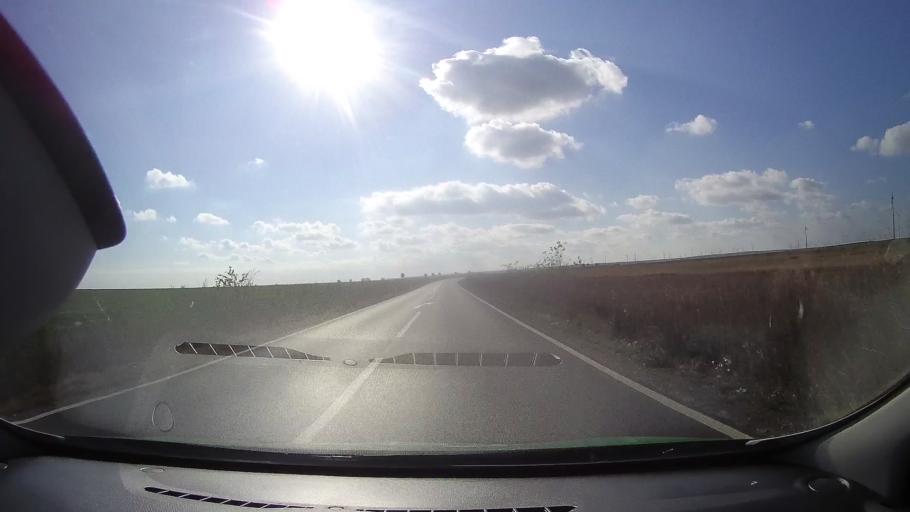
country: RO
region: Constanta
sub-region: Comuna Mihai Viteazu
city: Mihai Viteazu
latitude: 44.6690
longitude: 28.6832
